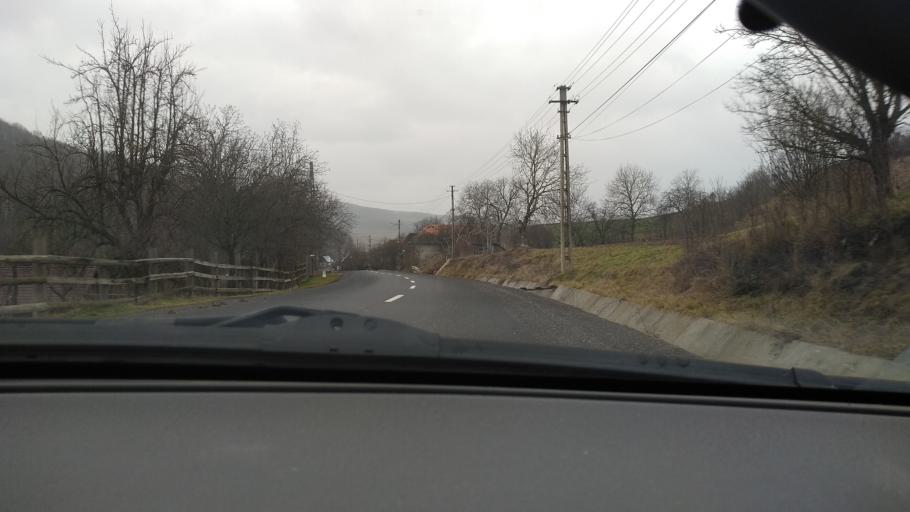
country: RO
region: Mures
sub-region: Comuna Magherani
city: Magherani
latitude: 46.5718
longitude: 24.9232
